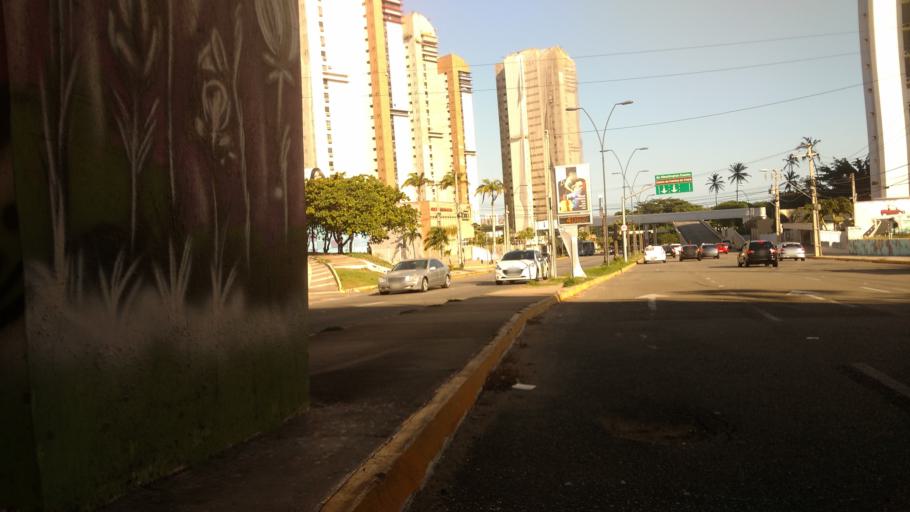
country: BR
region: Ceara
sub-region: Fortaleza
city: Fortaleza
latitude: -3.7483
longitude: -38.4928
